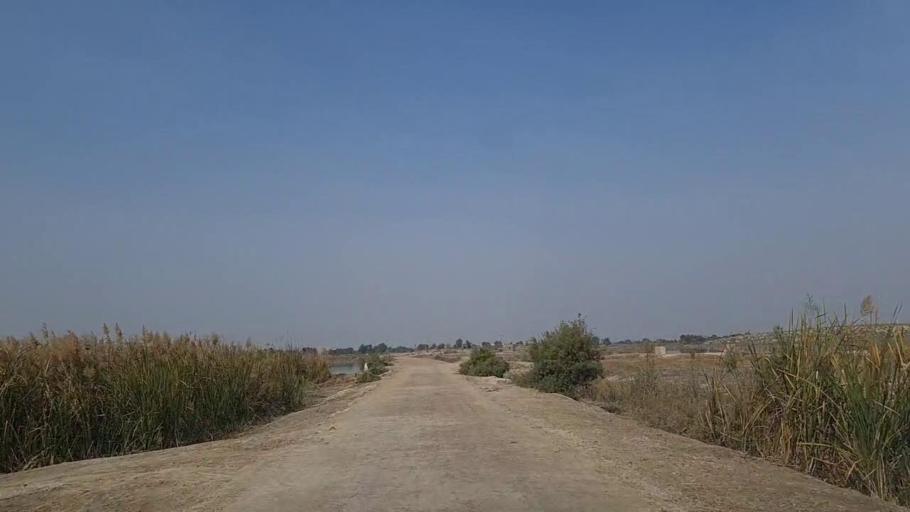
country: PK
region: Sindh
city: Daur
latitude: 26.5067
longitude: 68.4796
